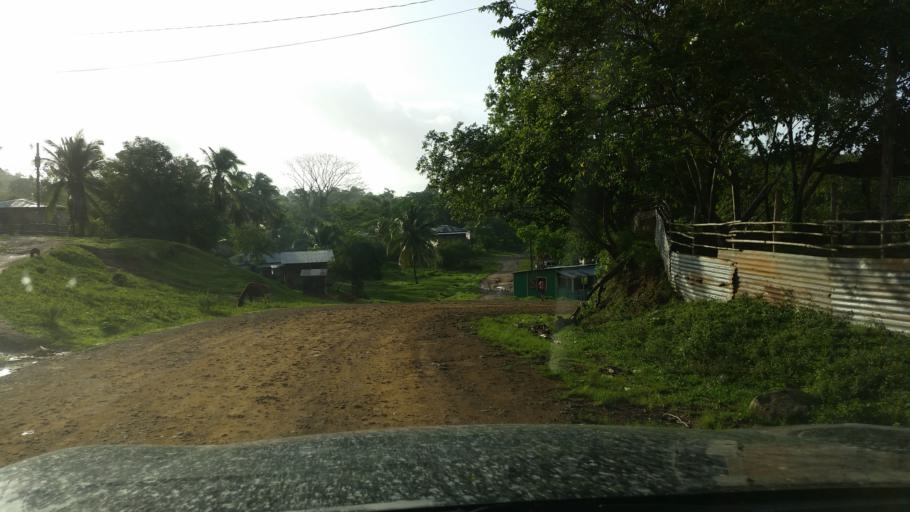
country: NI
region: Atlantico Norte (RAAN)
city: Puerto Cabezas
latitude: 14.0692
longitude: -83.9874
